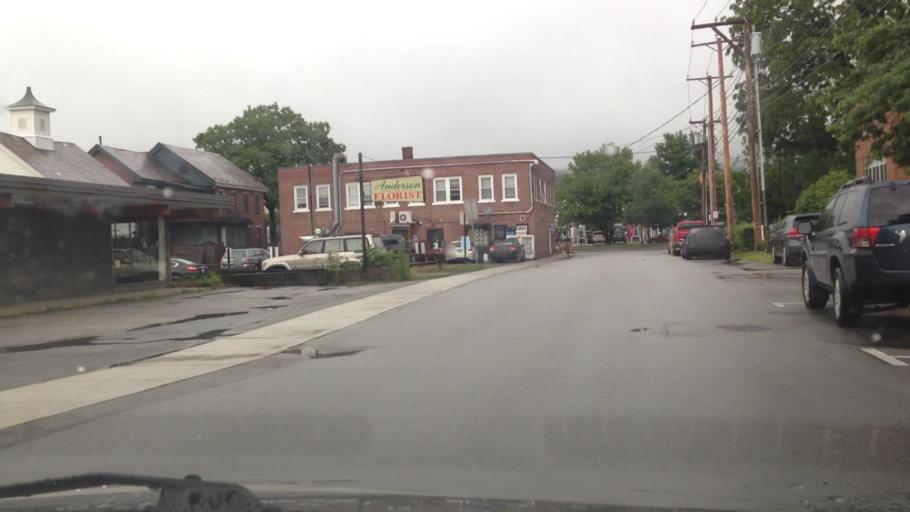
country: US
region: New Hampshire
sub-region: Cheshire County
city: Keene
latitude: 42.9300
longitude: -72.2791
